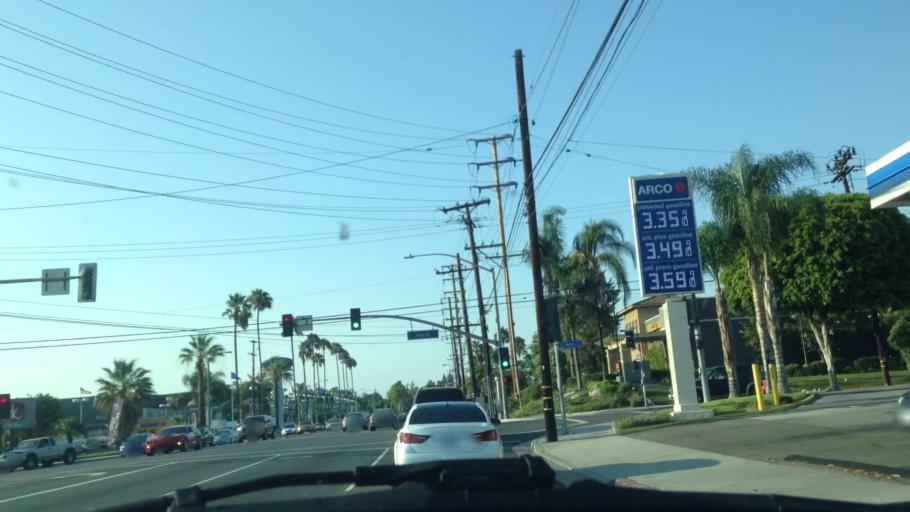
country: US
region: California
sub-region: Orange County
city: Villa Park
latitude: 33.8298
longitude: -117.8361
